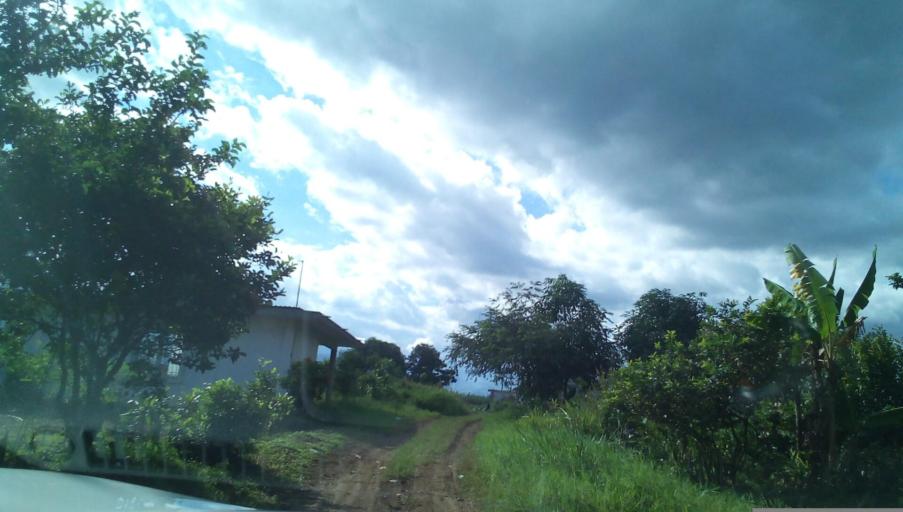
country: MX
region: Veracruz
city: Amatlan de los Reyes
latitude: 18.8262
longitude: -96.9218
